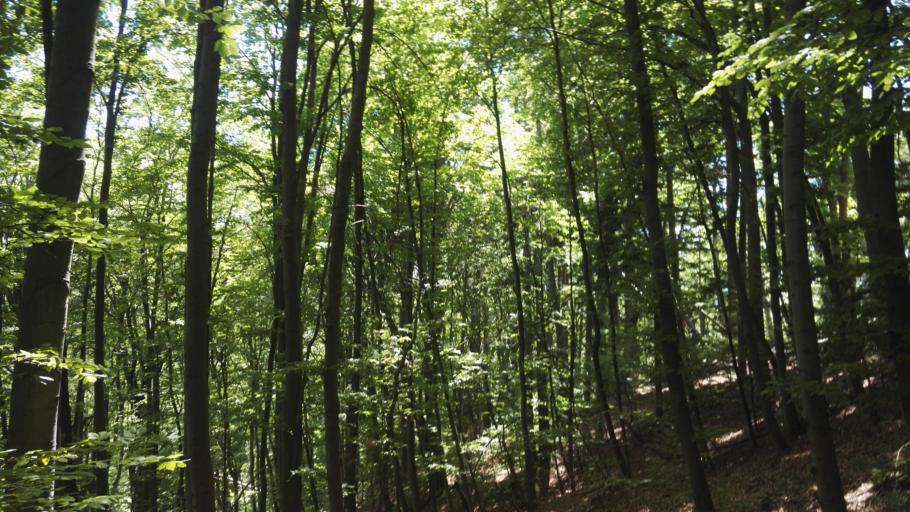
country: AT
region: Styria
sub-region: Graz Stadt
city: Goesting
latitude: 47.0882
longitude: 15.3892
